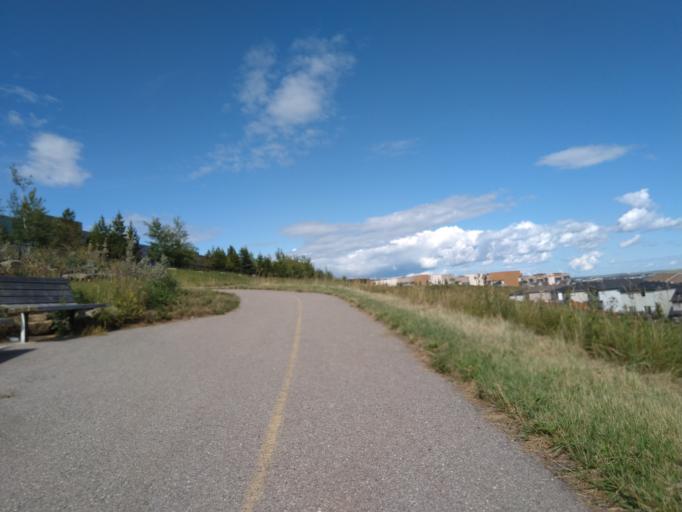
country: CA
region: Alberta
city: Calgary
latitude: 51.1582
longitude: -114.1567
